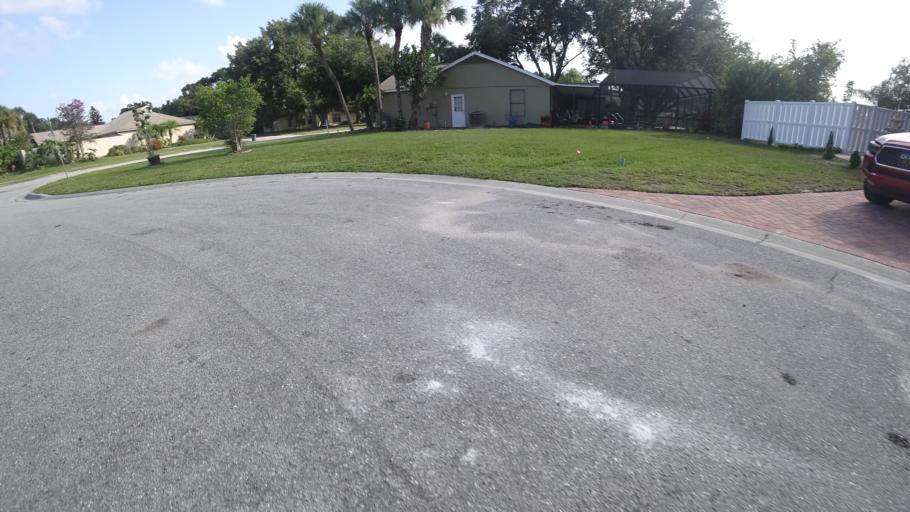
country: US
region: Florida
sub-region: Sarasota County
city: Desoto Lakes
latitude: 27.3928
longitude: -82.5021
